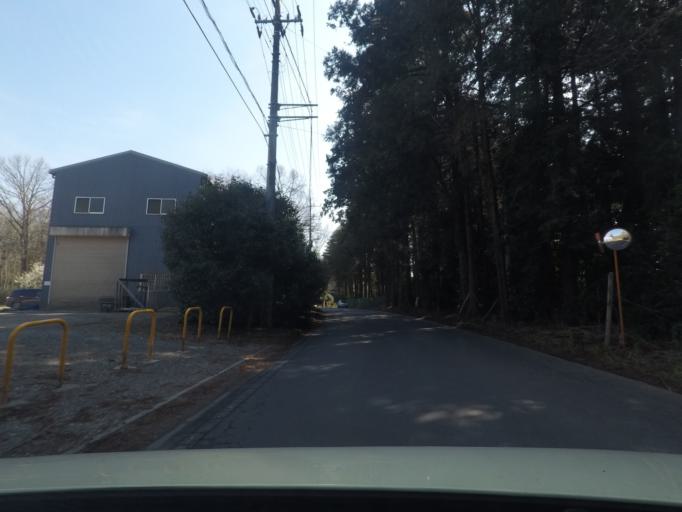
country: JP
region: Ibaraki
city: Ishioka
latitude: 36.1889
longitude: 140.3539
